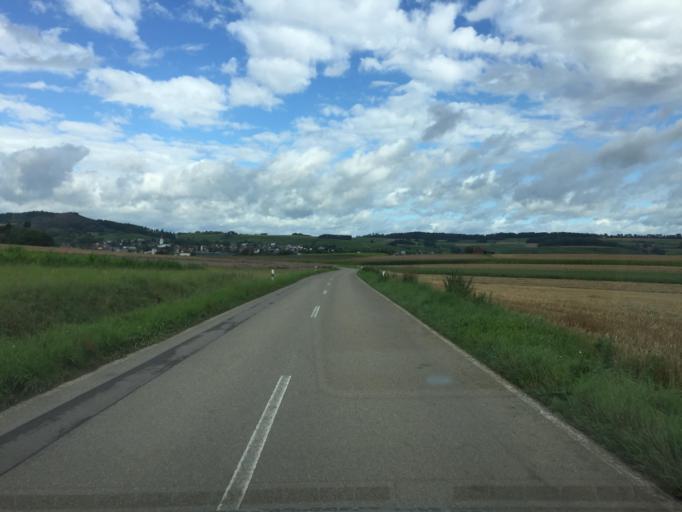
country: CH
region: Schaffhausen
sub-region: Bezirk Unterklettgau
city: Wilchingen
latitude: 47.6541
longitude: 8.4445
